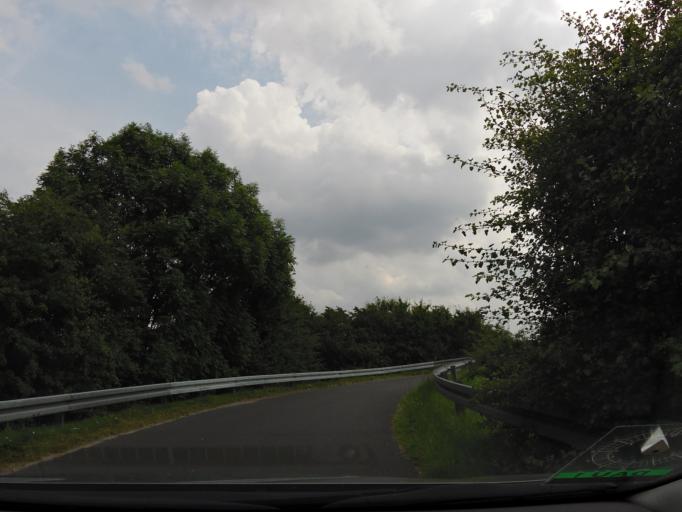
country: DK
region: South Denmark
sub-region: Odense Kommune
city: Neder Holluf
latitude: 55.3869
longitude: 10.4697
